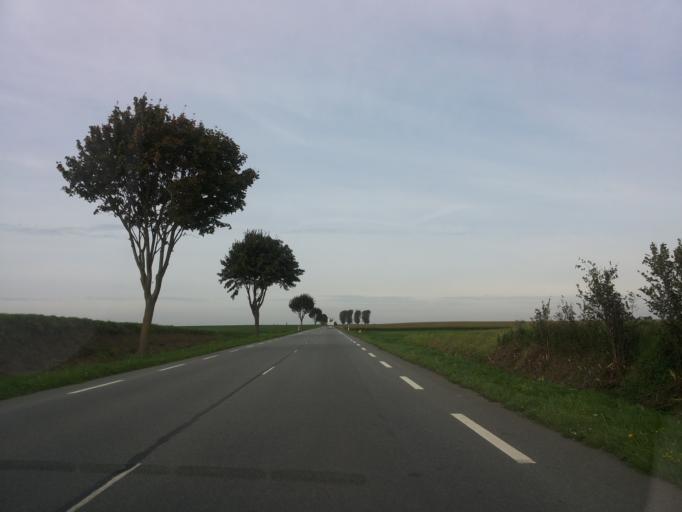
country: FR
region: Nord-Pas-de-Calais
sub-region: Departement du Nord
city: Lecluse
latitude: 50.2306
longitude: 3.0099
